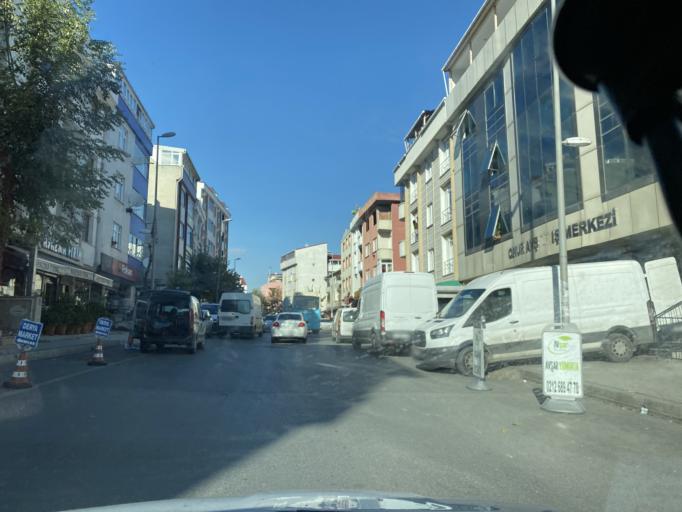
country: TR
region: Istanbul
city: Esenyurt
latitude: 41.0433
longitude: 28.6505
